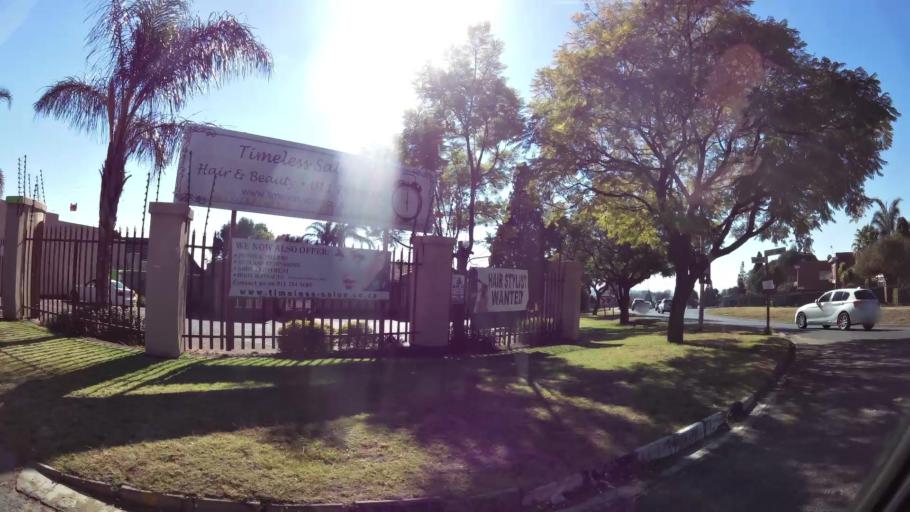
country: ZA
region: Gauteng
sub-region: City of Johannesburg Metropolitan Municipality
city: Roodepoort
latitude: -26.1239
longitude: 27.8471
